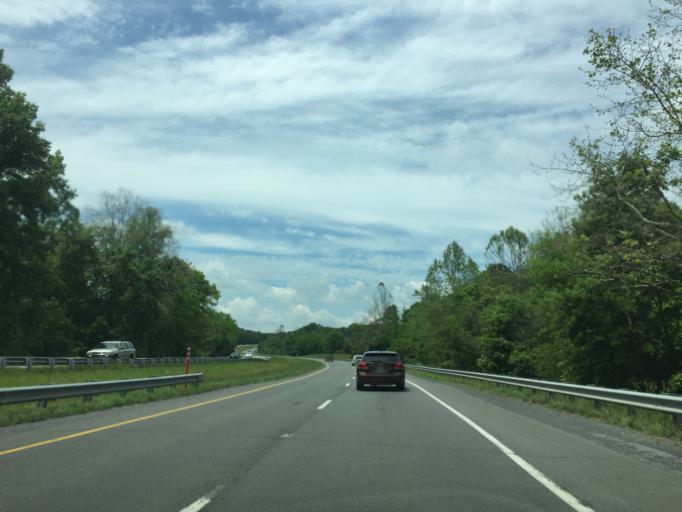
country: US
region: Virginia
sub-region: Frederick County
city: Shawnee Land
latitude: 39.2853
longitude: -78.2600
